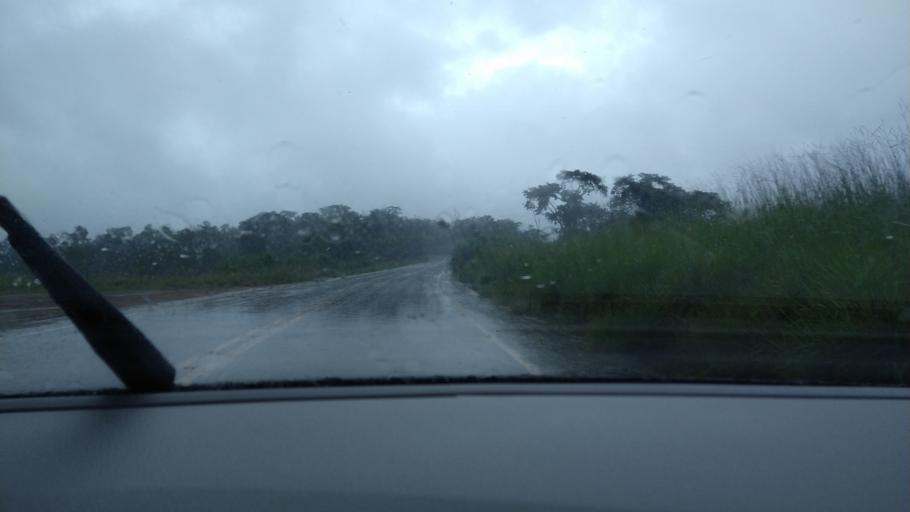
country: BR
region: Minas Gerais
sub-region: Ponte Nova
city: Ponte Nova
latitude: -20.5526
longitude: -42.8761
